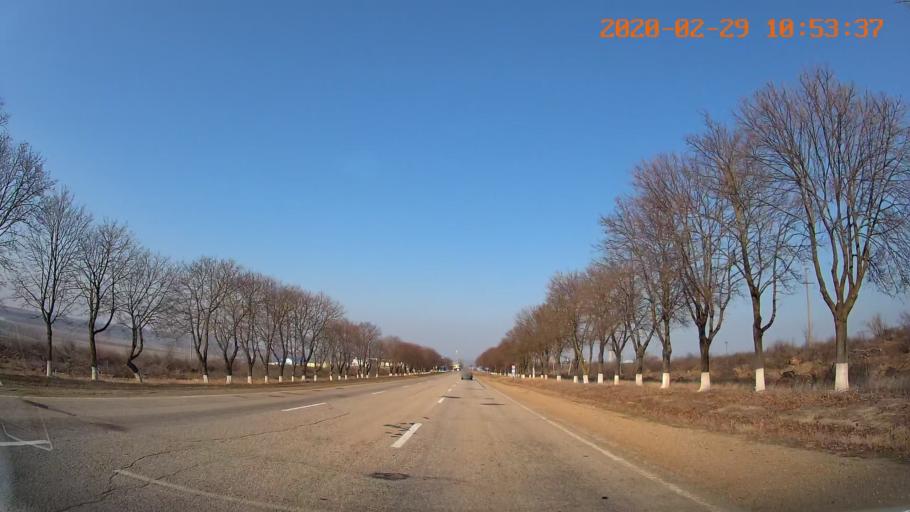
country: MD
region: Telenesti
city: Grigoriopol
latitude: 47.1174
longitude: 29.3330
